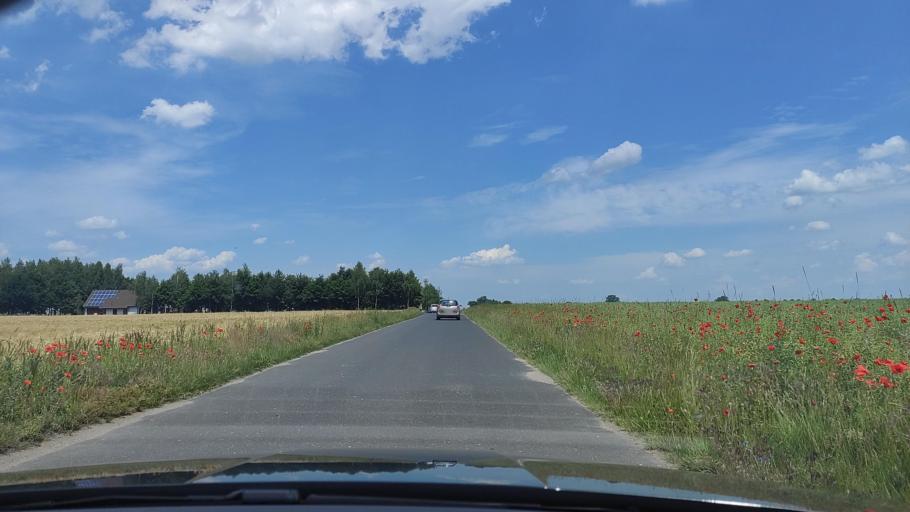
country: PL
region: Greater Poland Voivodeship
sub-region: Powiat gnieznienski
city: Lubowo
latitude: 52.5263
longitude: 17.3851
